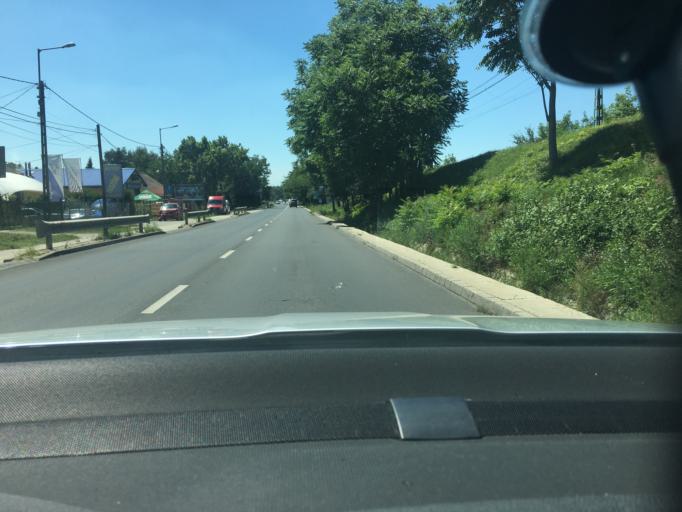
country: HU
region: Pest
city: Csomor
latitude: 47.5283
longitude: 19.2323
